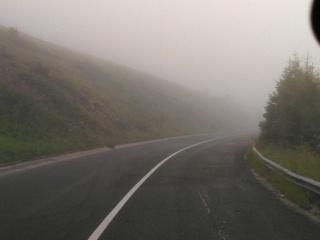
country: BG
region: Lovech
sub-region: Obshtina Troyan
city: Troyan
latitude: 42.7773
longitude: 24.6095
